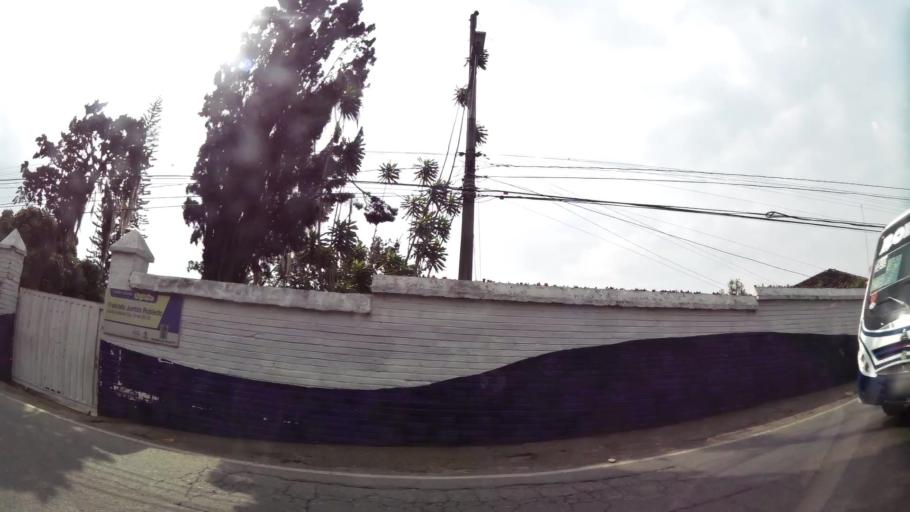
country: CO
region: Antioquia
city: Medellin
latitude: 6.2778
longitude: -75.5979
